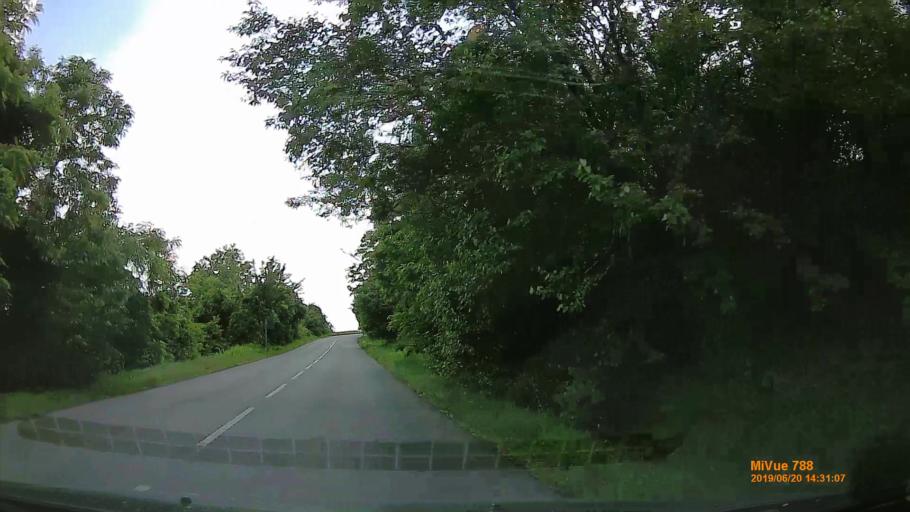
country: HU
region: Baranya
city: Hosszuheteny
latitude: 46.1425
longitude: 18.3488
